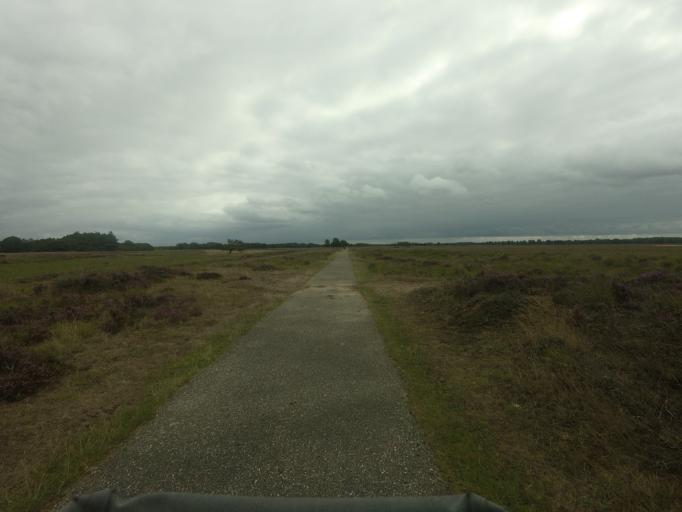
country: NL
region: Friesland
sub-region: Gemeente Weststellingwerf
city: Noordwolde
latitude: 52.9056
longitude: 6.2587
